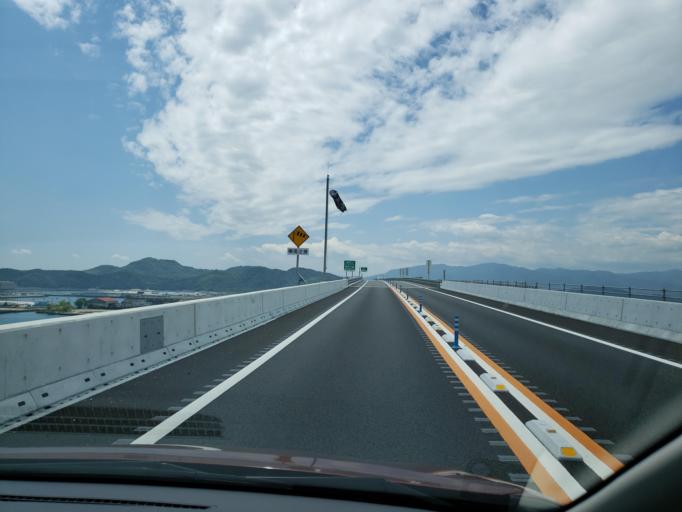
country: JP
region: Tokushima
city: Tokushima-shi
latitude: 34.0564
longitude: 134.5887
